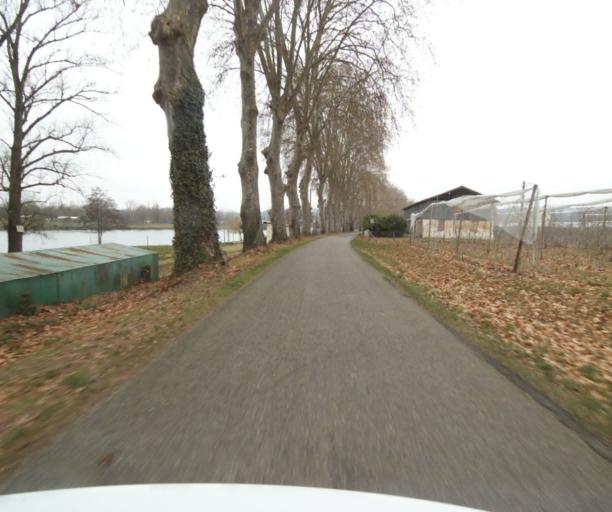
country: FR
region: Midi-Pyrenees
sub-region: Departement du Tarn-et-Garonne
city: Moissac
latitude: 44.0947
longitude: 1.0958
